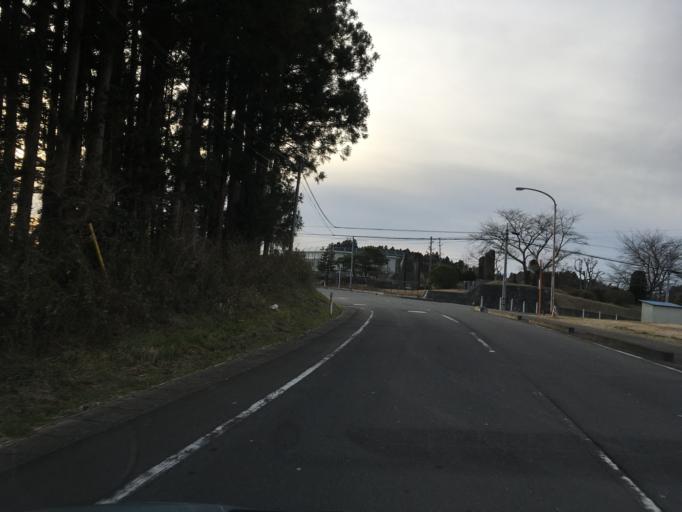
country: JP
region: Miyagi
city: Wakuya
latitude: 38.7004
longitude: 141.1117
